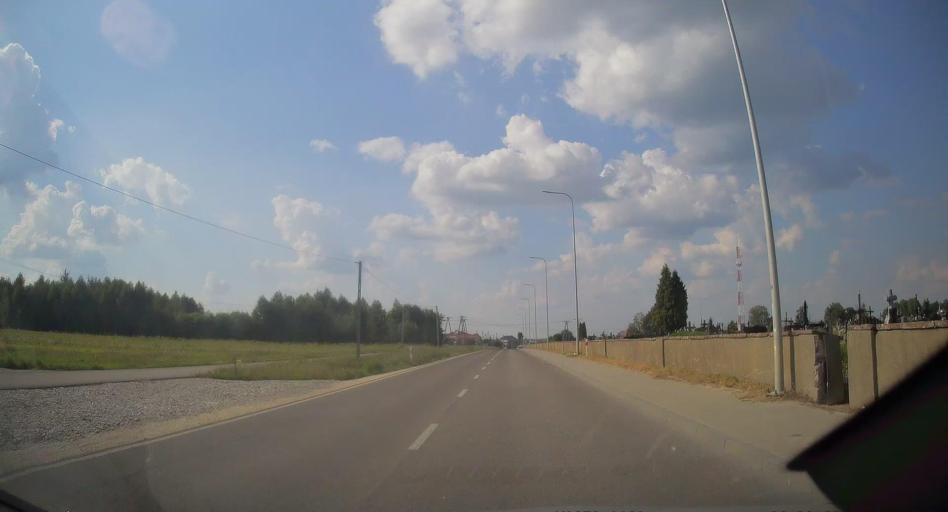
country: PL
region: Swietokrzyskie
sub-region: Powiat konecki
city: Radoszyce
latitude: 51.0680
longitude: 20.2705
